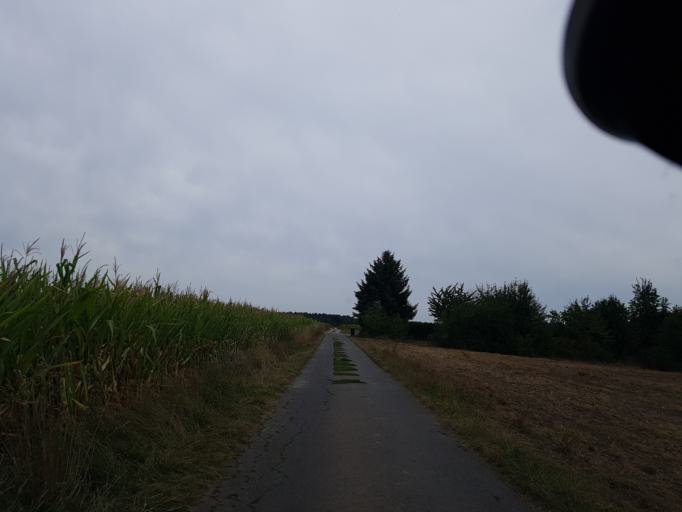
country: DE
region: Brandenburg
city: Finsterwalde
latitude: 51.6105
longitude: 13.6618
